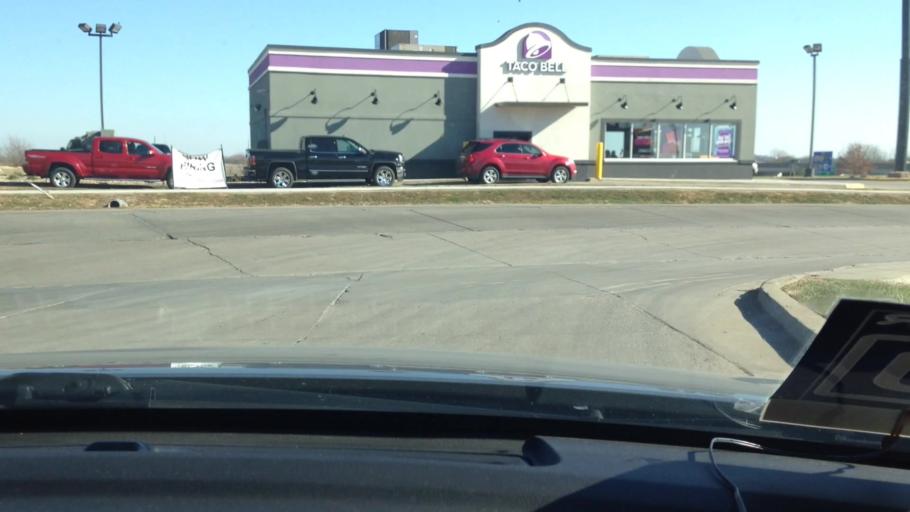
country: US
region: Missouri
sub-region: Platte County
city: Platte City
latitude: 39.3545
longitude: -94.7649
